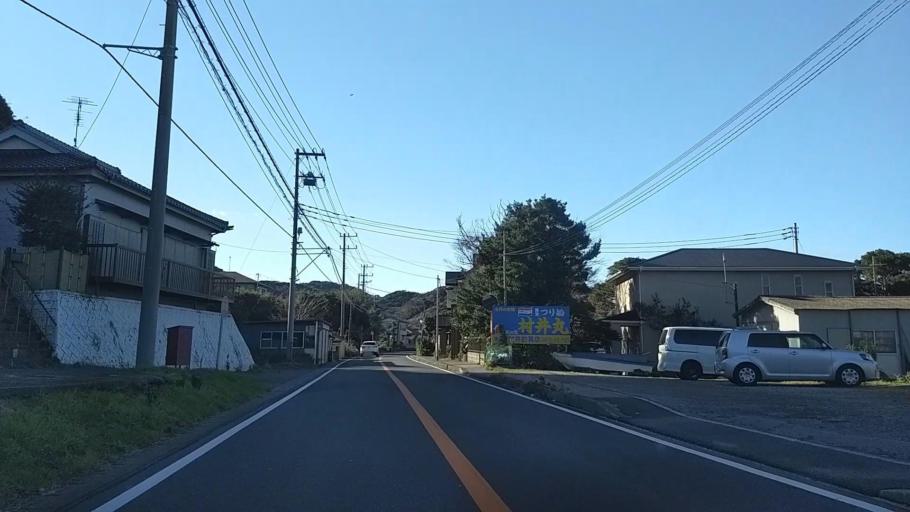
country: JP
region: Chiba
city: Futtsu
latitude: 35.2007
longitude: 139.8306
